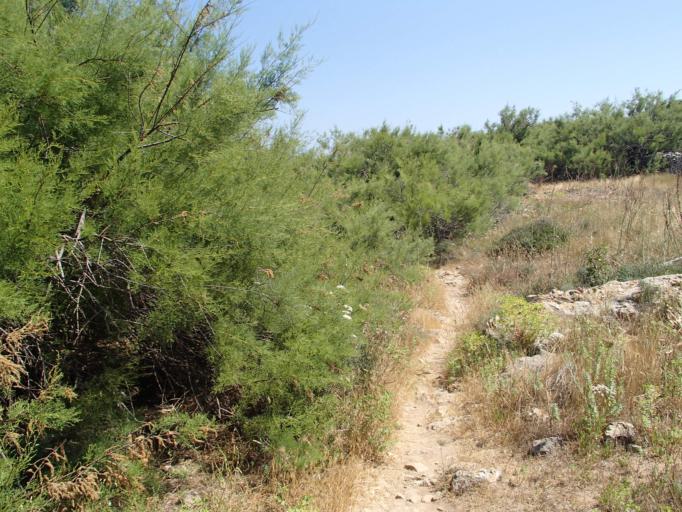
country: ES
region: Balearic Islands
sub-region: Illes Balears
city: Es Castell
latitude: 39.8585
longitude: 4.3051
